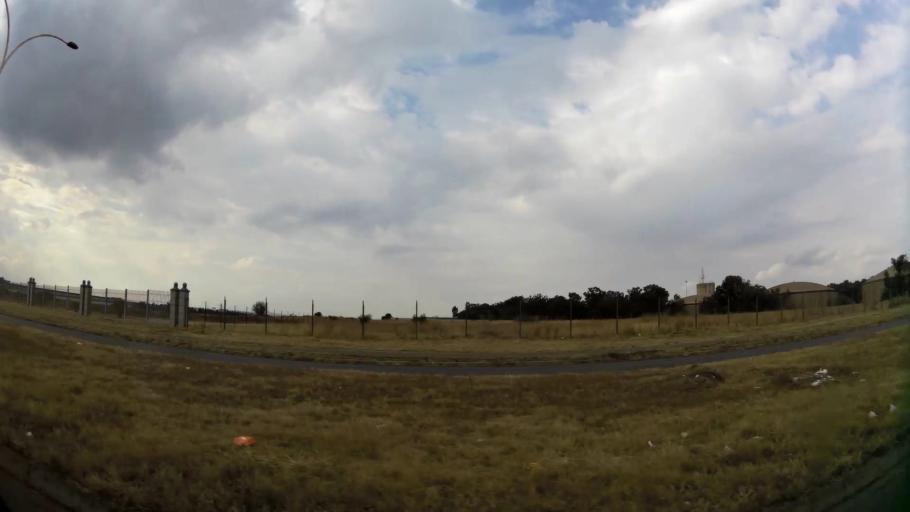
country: ZA
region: Gauteng
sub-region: Sedibeng District Municipality
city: Vanderbijlpark
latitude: -26.6849
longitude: 27.8210
